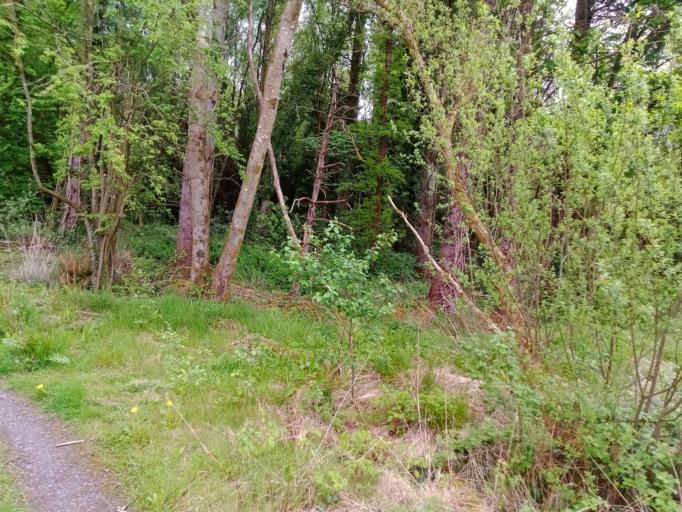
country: IE
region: Leinster
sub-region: Kilkenny
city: Castlecomer
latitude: 52.8155
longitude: -7.2022
